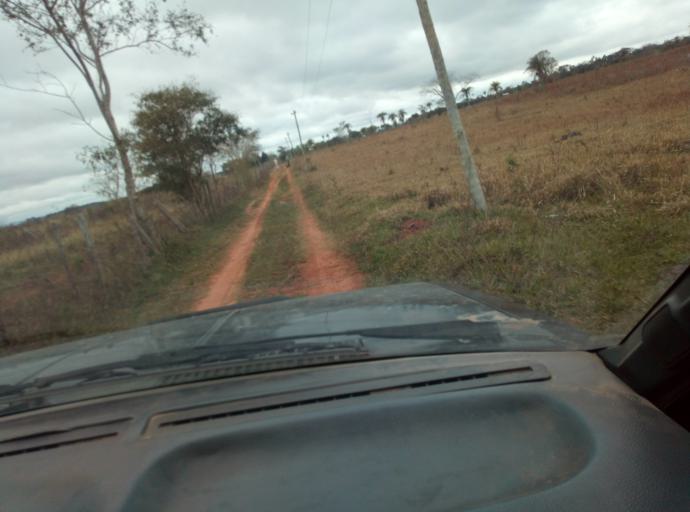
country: PY
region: Caaguazu
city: Doctor Cecilio Baez
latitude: -25.1446
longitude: -56.2968
